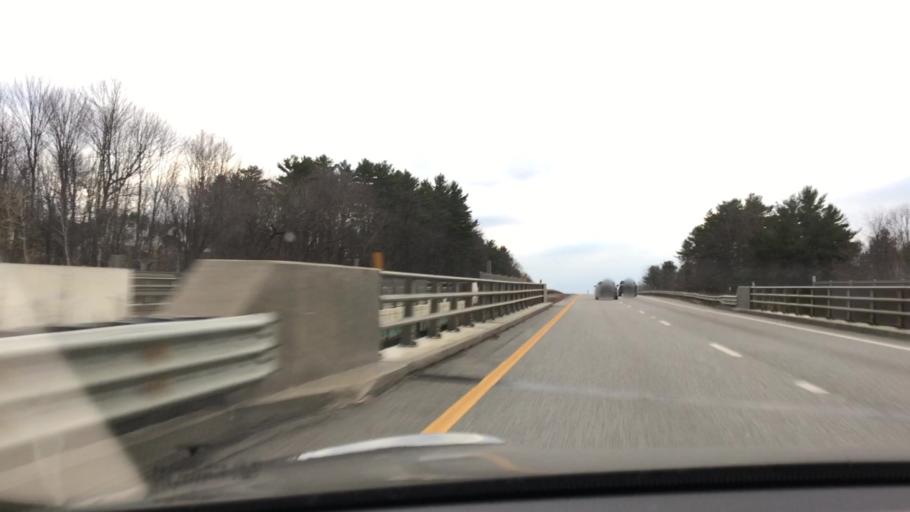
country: US
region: Maine
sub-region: Kennebec County
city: Hallowell
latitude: 44.2893
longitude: -69.8070
